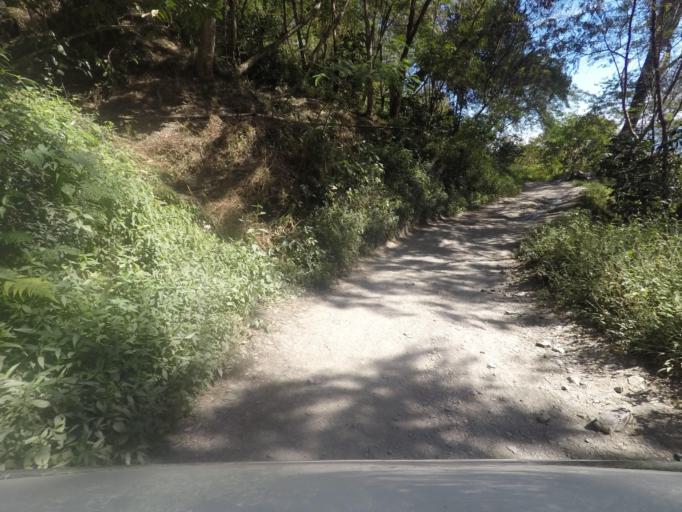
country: TL
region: Ermera
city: Gleno
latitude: -8.7290
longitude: 125.3358
